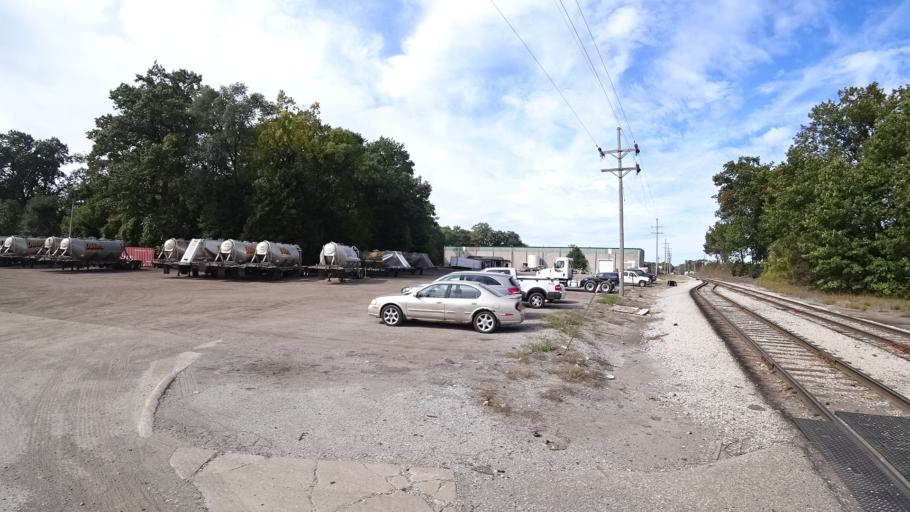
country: US
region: Indiana
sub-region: LaPorte County
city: Trail Creek
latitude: 41.7115
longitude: -86.8648
